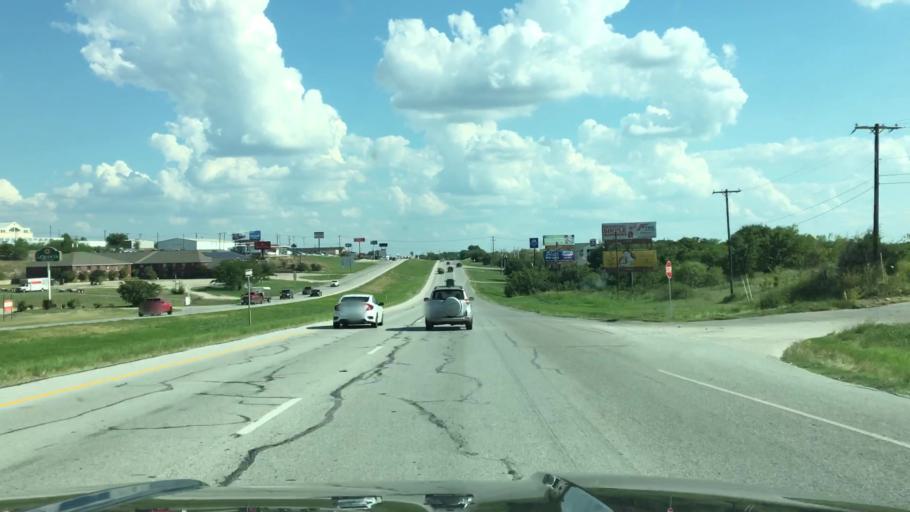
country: US
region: Texas
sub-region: Wise County
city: Decatur
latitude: 33.2251
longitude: -97.5919
